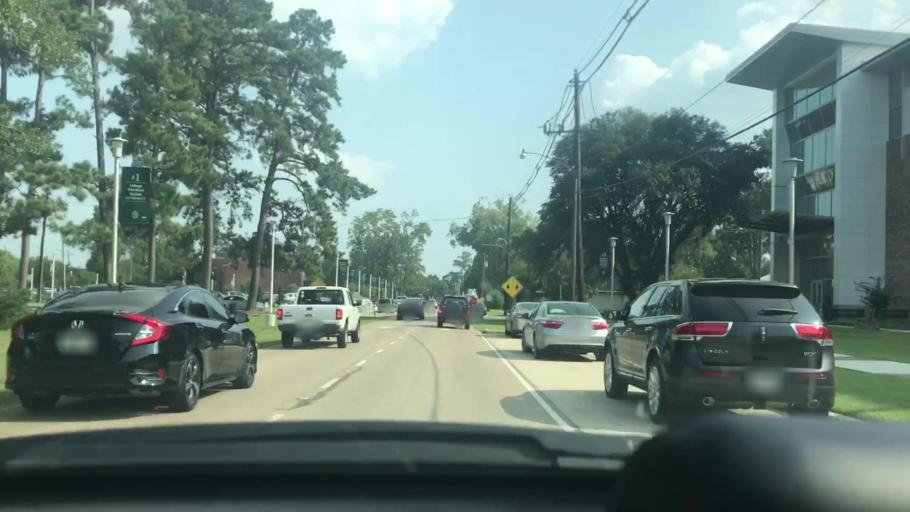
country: US
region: Louisiana
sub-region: Tangipahoa Parish
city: Hammond
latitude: 30.5113
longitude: -90.4646
